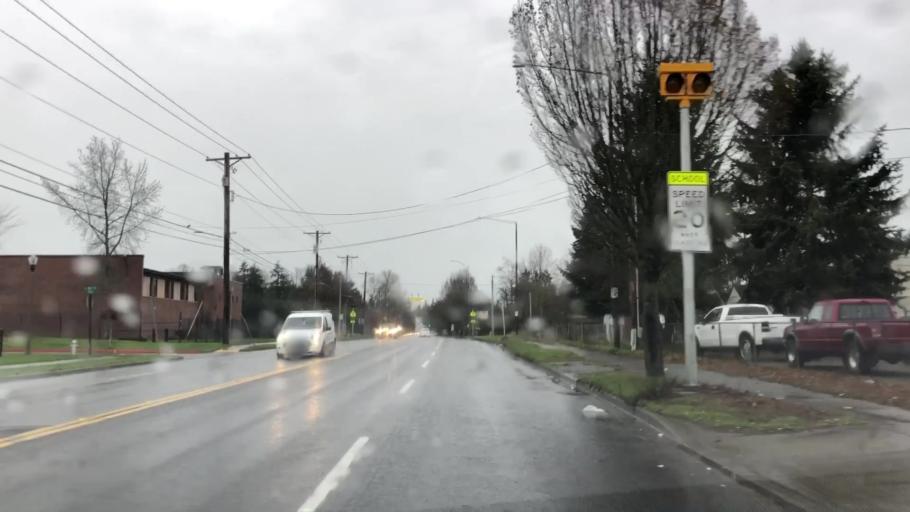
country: US
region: Washington
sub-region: Pierce County
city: Waller
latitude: 47.2114
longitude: -122.4080
